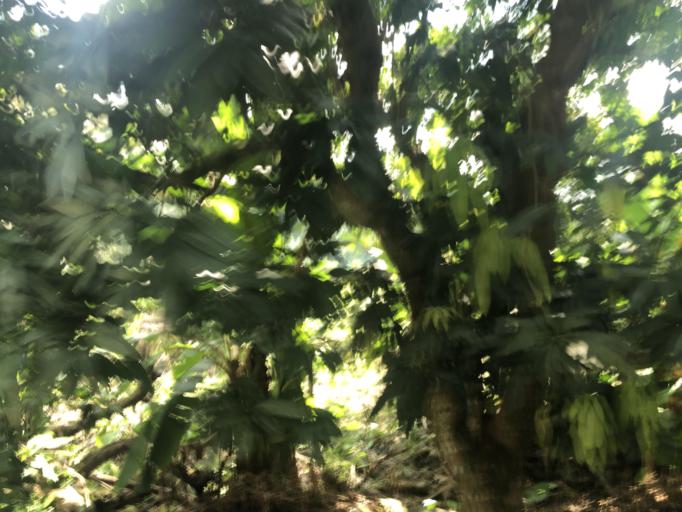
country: TW
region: Taiwan
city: Yujing
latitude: 22.9333
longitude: 120.5890
